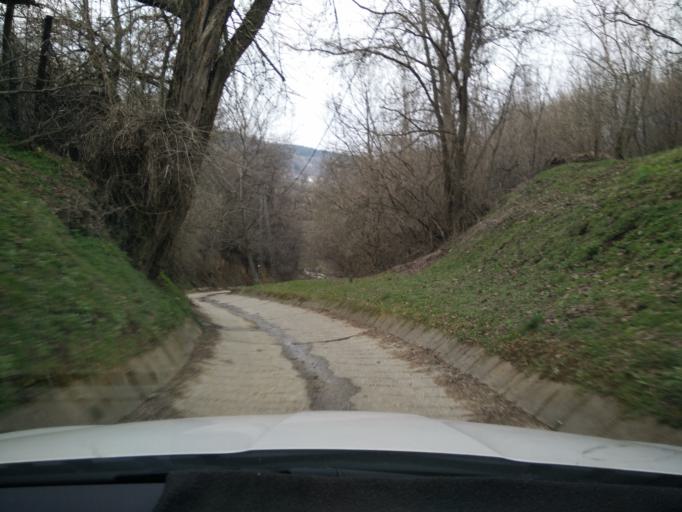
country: HU
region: Tolna
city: Szekszard
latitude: 46.3490
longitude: 18.6751
